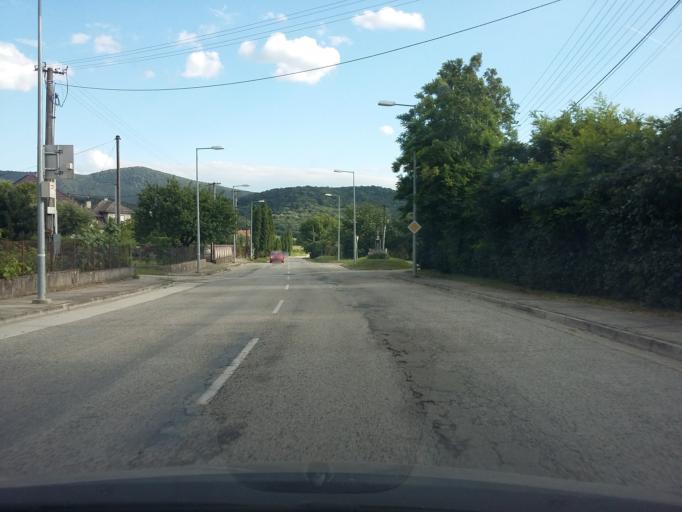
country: SK
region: Trnavsky
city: Smolenice
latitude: 48.5540
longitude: 17.3498
